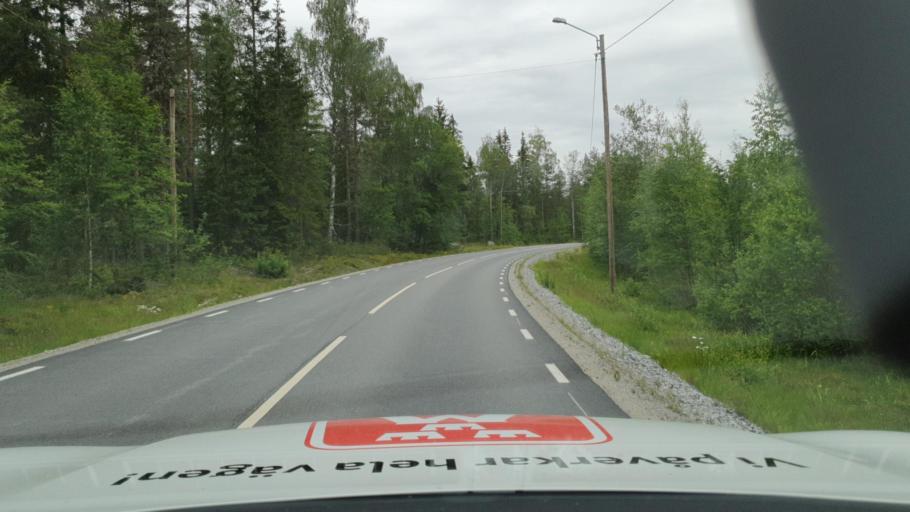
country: SE
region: Vaesterbotten
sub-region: Nordmalings Kommun
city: Nordmaling
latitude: 63.5061
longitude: 19.3306
